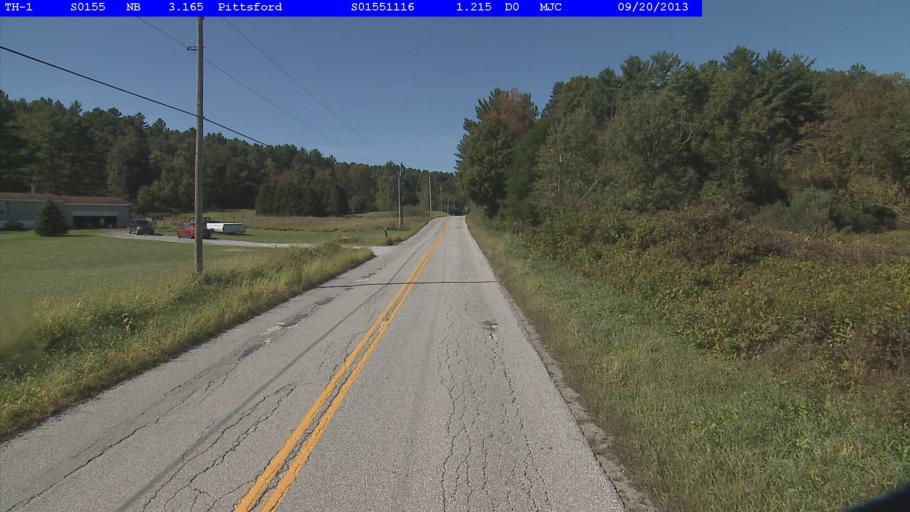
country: US
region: Vermont
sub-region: Rutland County
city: Brandon
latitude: 43.7073
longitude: -73.0521
